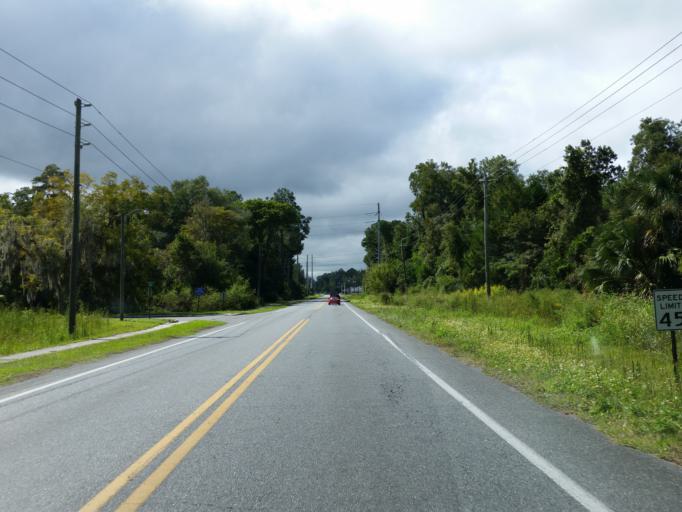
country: US
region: Florida
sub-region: Columbia County
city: Five Points
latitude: 30.2033
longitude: -82.6314
